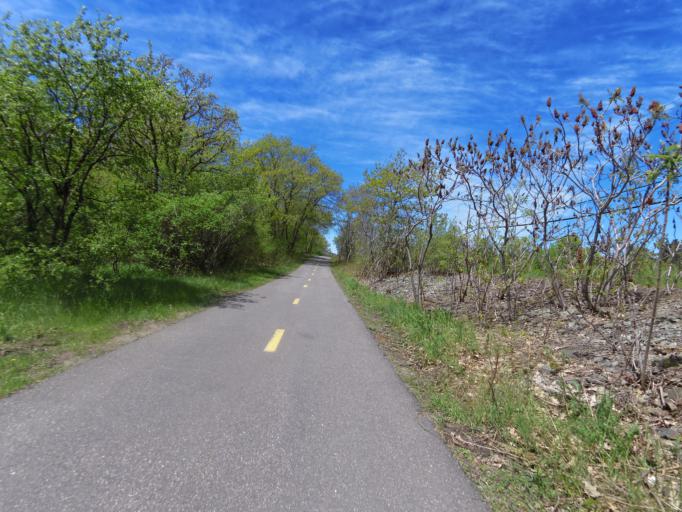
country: CA
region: Ontario
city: Bells Corners
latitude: 45.3842
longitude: -75.8204
